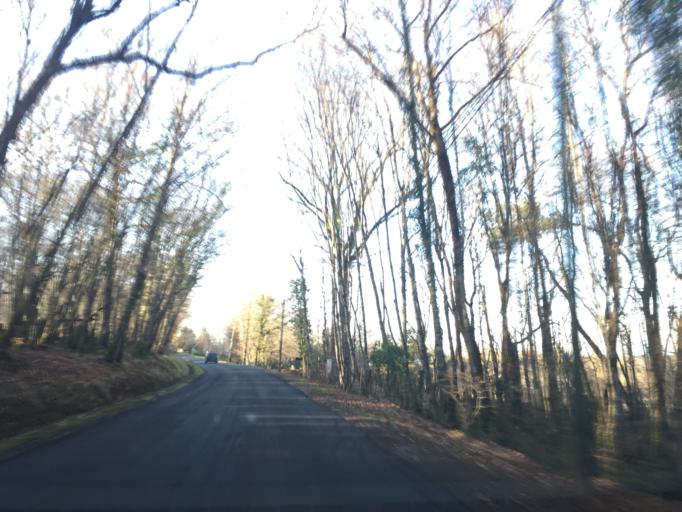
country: FR
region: Aquitaine
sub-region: Departement de la Dordogne
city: Neuvic
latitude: 45.1361
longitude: 0.4878
